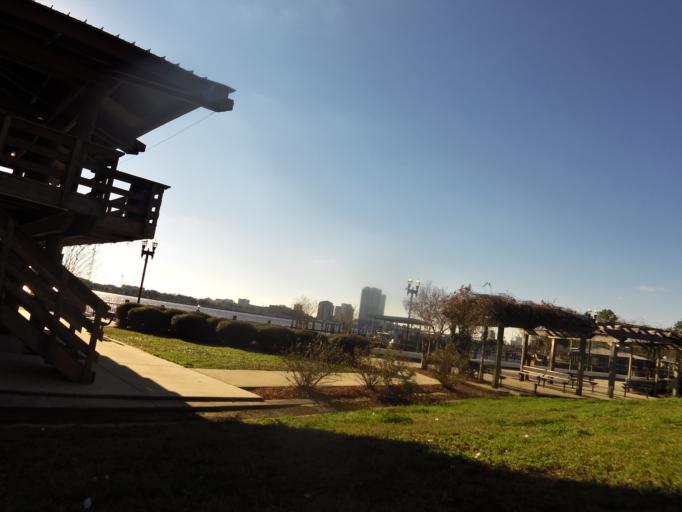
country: US
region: Florida
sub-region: Duval County
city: Jacksonville
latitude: 30.3196
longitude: -81.6387
